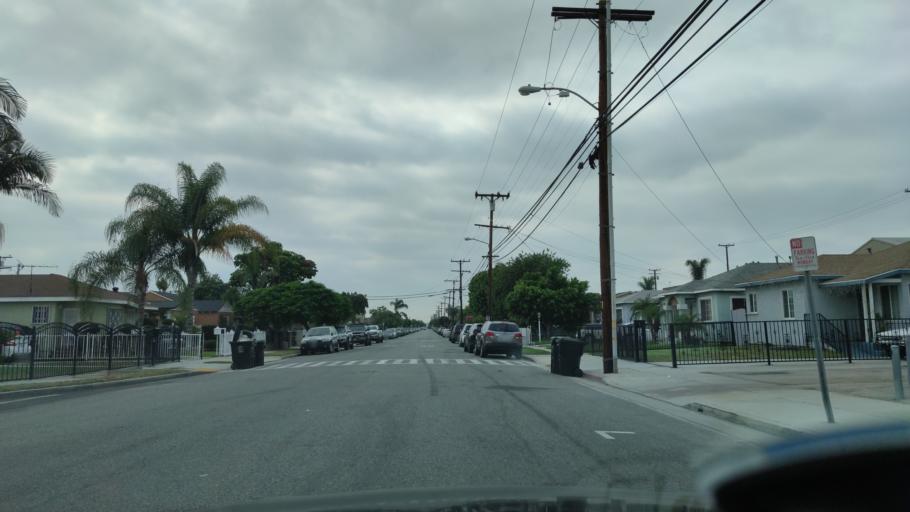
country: US
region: California
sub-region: Los Angeles County
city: Maywood
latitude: 33.9940
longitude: -118.1858
